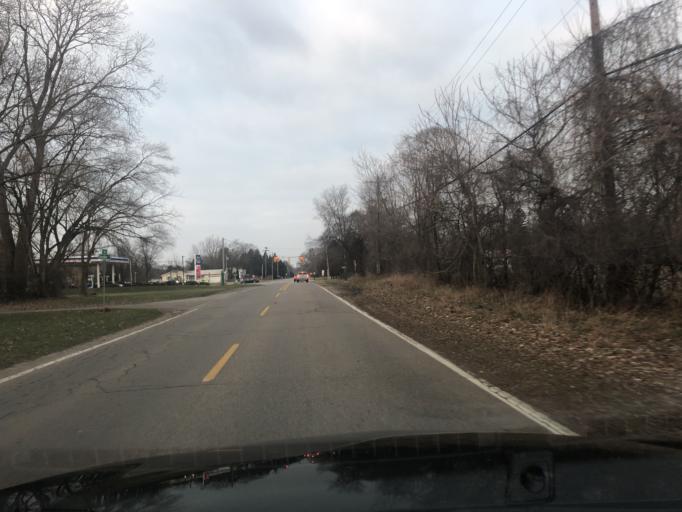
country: US
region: Michigan
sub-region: Wayne County
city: Romulus
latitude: 42.2377
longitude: -83.3842
